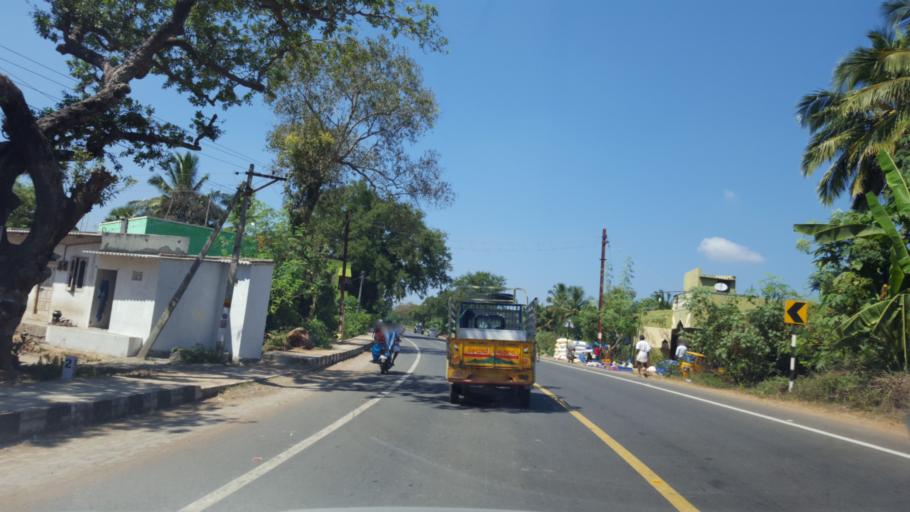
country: IN
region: Tamil Nadu
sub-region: Kancheepuram
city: Karumbakkam
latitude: 12.6429
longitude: 80.0415
